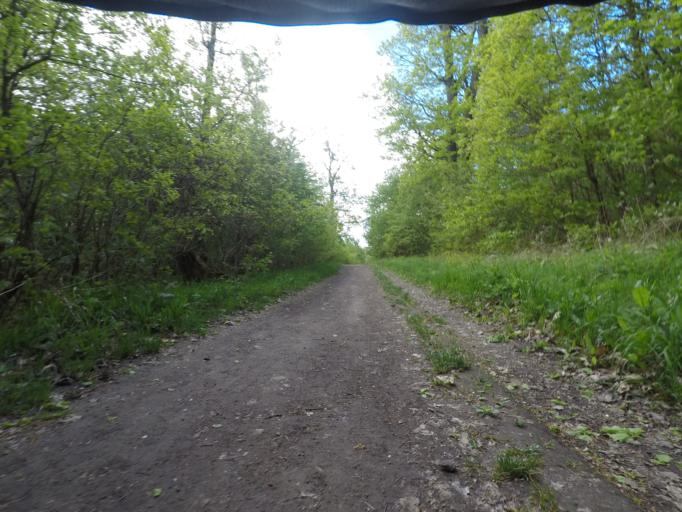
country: AT
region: Lower Austria
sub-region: Politischer Bezirk Modling
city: Perchtoldsdorf
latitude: 48.1725
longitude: 16.2657
